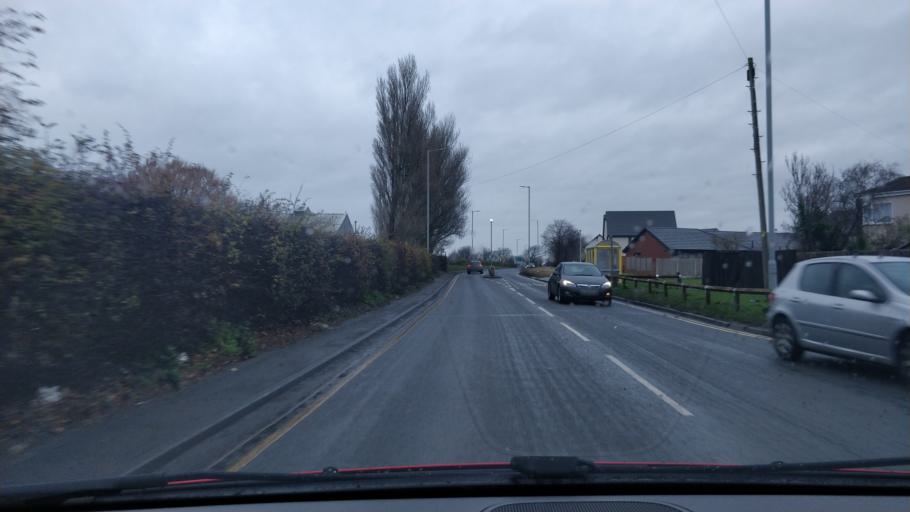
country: GB
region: England
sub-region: Sefton
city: Thornton
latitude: 53.4934
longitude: -2.9858
